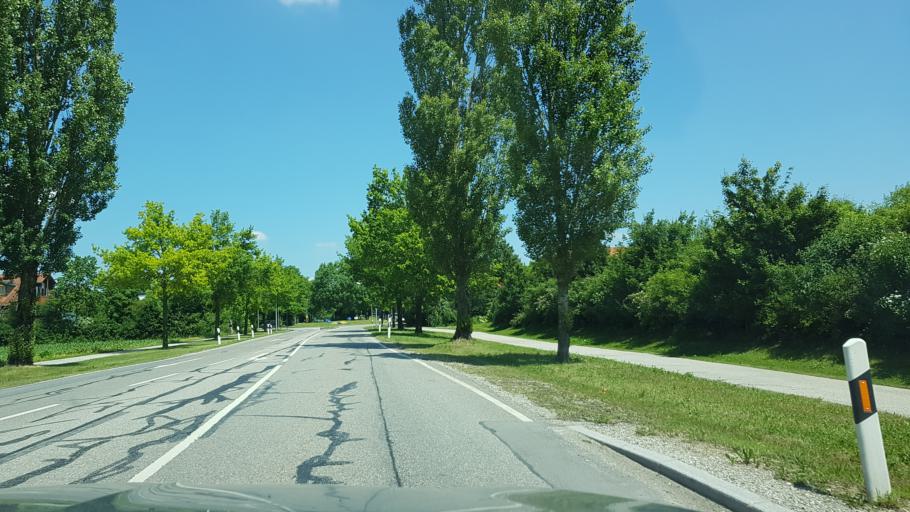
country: DE
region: Bavaria
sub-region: Upper Bavaria
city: Aschheim
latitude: 48.1660
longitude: 11.7107
